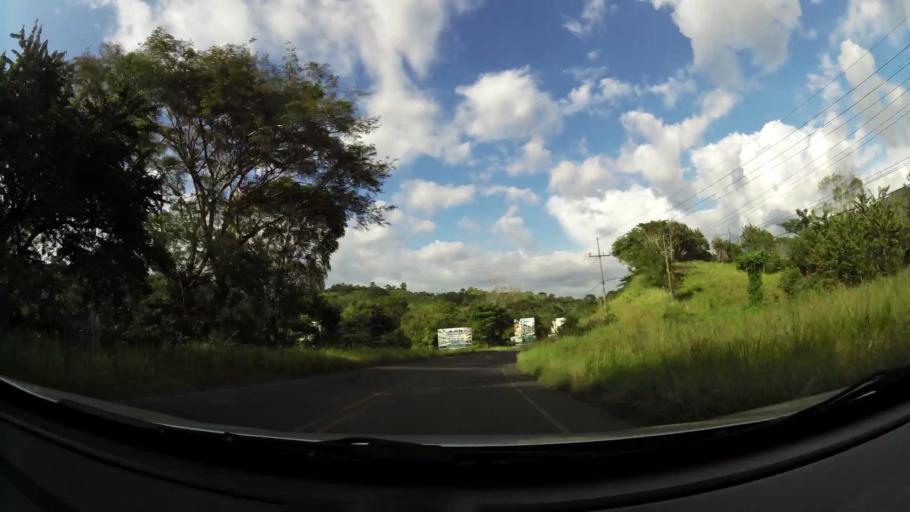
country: CR
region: Puntarenas
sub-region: Canton de Garabito
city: Jaco
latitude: 9.7197
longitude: -84.6319
